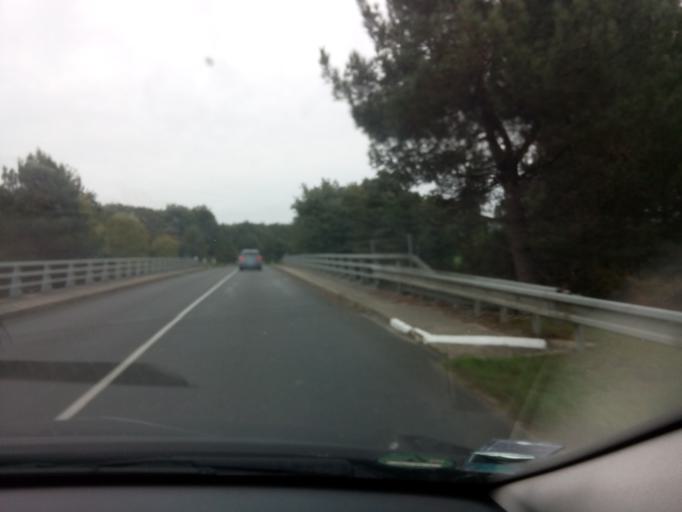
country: FR
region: Pays de la Loire
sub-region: Departement de Maine-et-Loire
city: Seiches-sur-le-Loir
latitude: 47.5554
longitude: -0.3335
